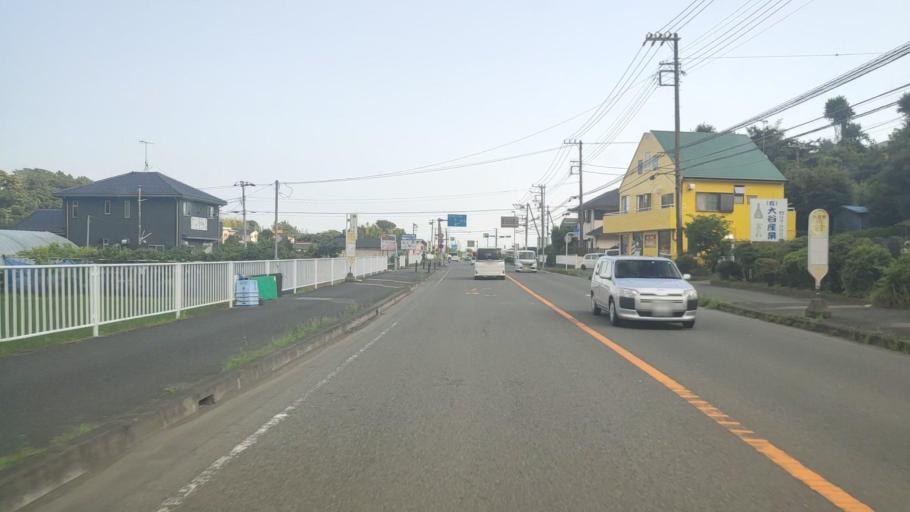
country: JP
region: Kanagawa
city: Isehara
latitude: 35.3805
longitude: 139.3173
